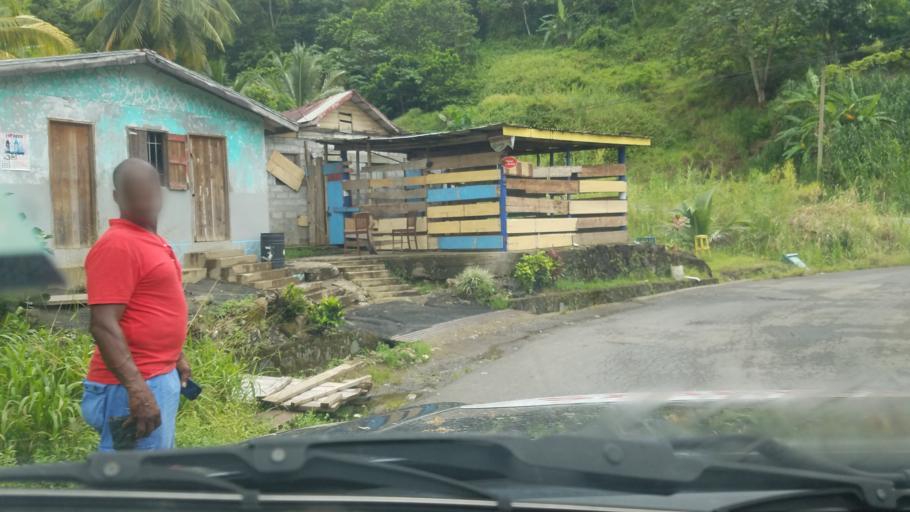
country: LC
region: Anse-la-Raye
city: Anse La Raye
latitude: 13.9258
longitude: -60.9932
